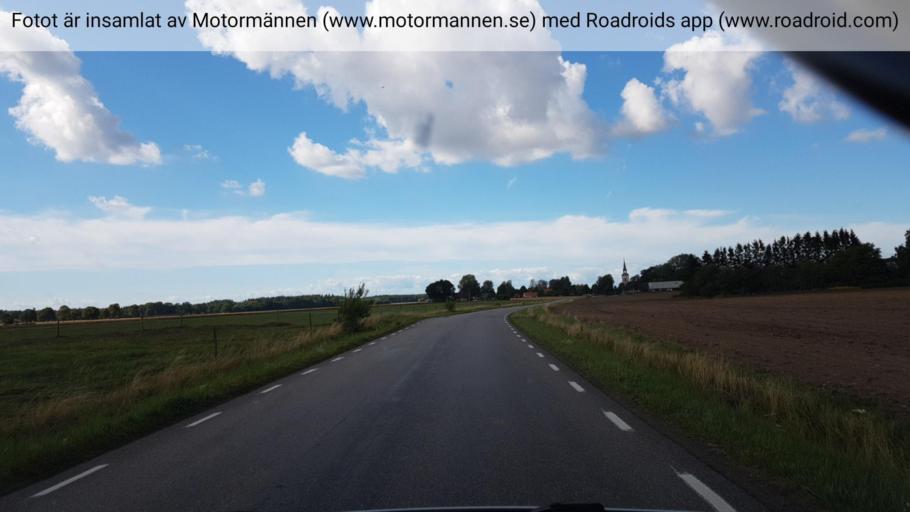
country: SE
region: Vaestra Goetaland
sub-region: Gotene Kommun
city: Kallby
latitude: 58.4662
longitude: 13.3317
